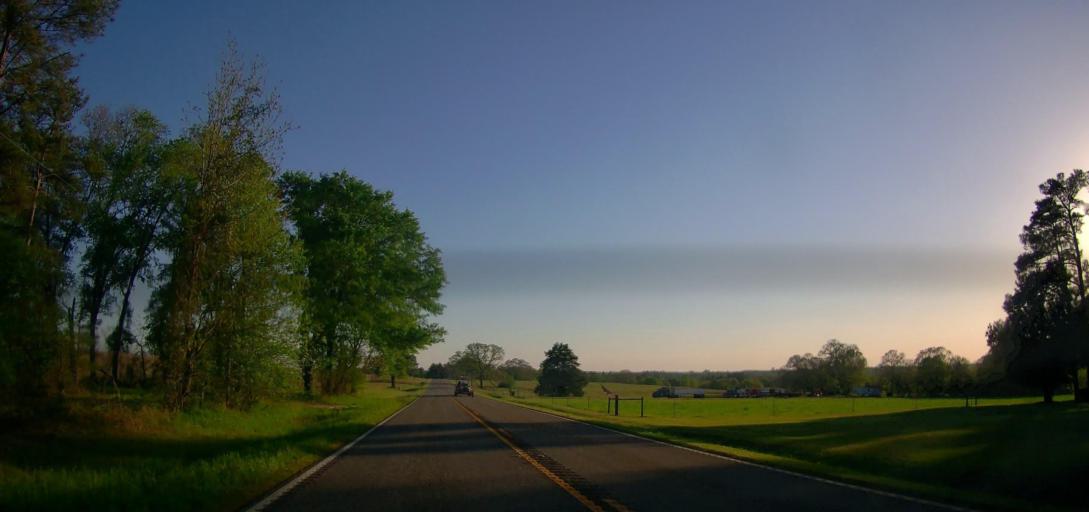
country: US
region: Georgia
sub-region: Marion County
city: Buena Vista
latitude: 32.4037
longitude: -84.4400
